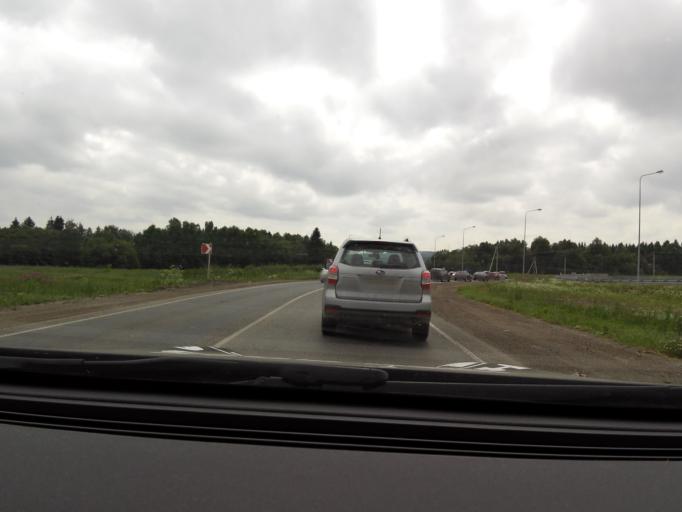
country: RU
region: Perm
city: Zvezdnyy
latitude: 57.7809
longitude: 56.3449
